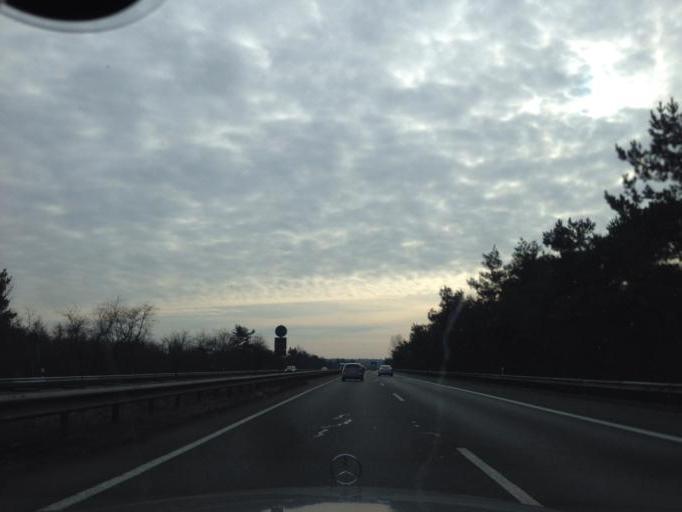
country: DE
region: Lower Saxony
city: Holdorf
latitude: 52.5636
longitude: 8.1122
